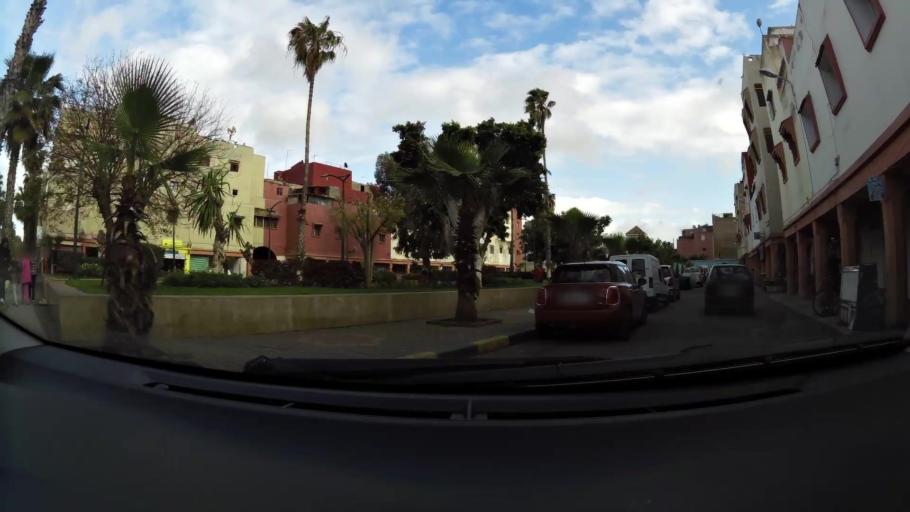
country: MA
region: Grand Casablanca
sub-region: Mohammedia
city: Mohammedia
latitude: 33.7010
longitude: -7.3810
